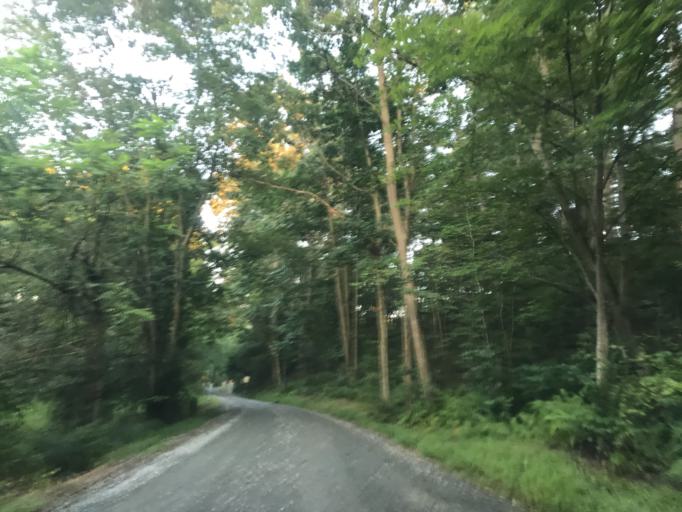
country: US
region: Maryland
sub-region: Harford County
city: Jarrettsville
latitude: 39.6751
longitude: -76.5380
